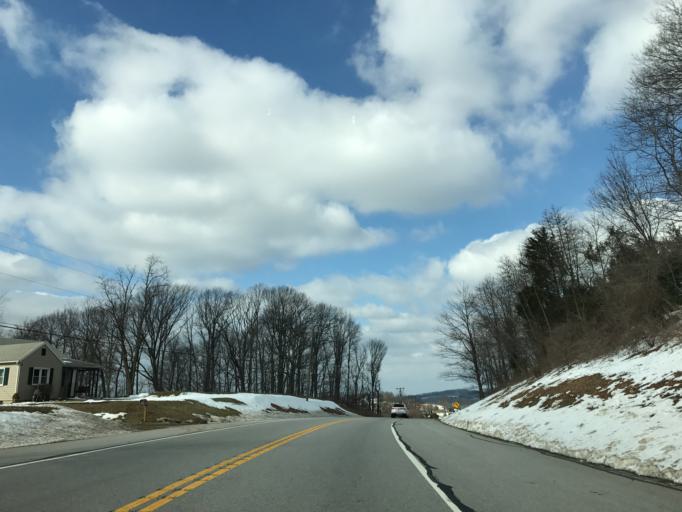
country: US
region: Maryland
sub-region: Carroll County
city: Manchester
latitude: 39.7118
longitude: -76.9175
